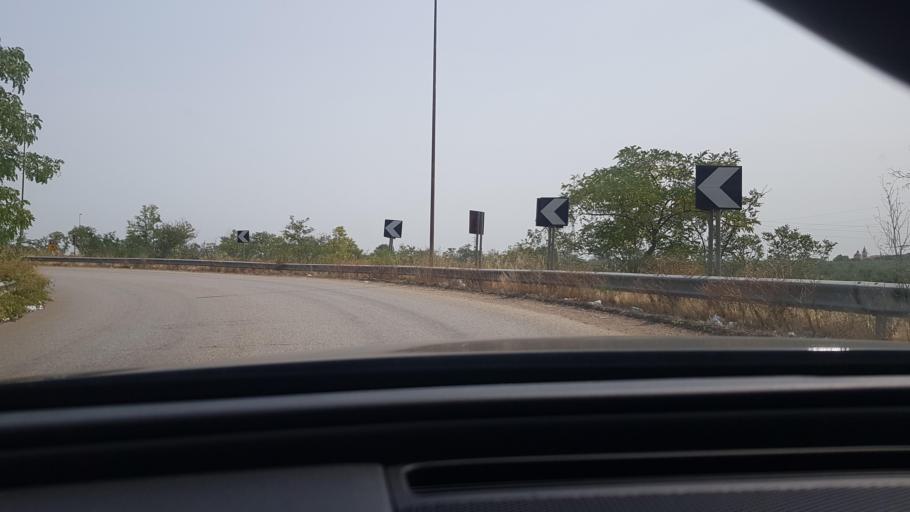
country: IT
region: Apulia
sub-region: Provincia di Barletta - Andria - Trani
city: Andria
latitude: 41.2142
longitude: 16.2657
